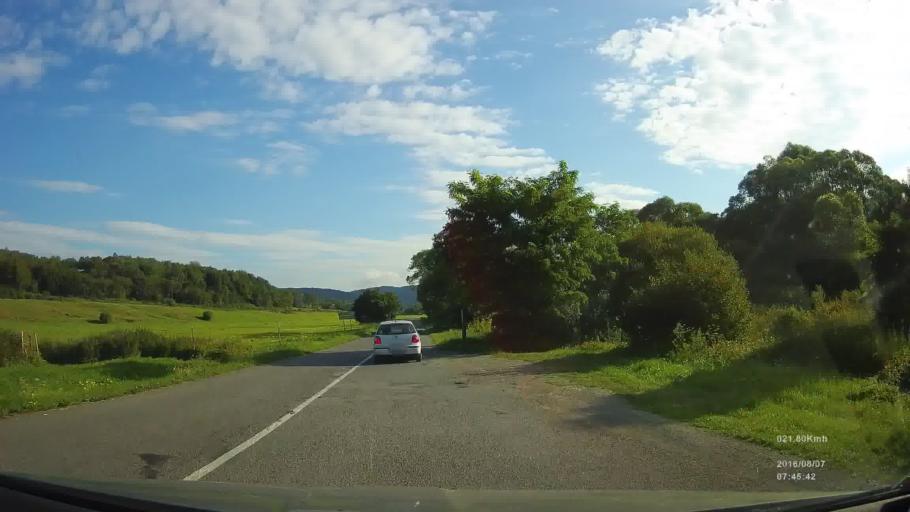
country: SK
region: Presovsky
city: Stropkov
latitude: 49.2619
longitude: 21.7454
